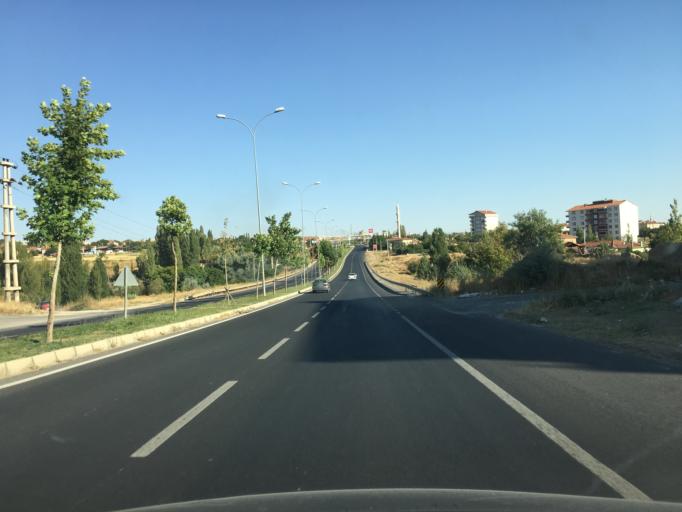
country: TR
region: Kirsehir
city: Kirsehir
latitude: 39.1375
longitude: 34.1827
